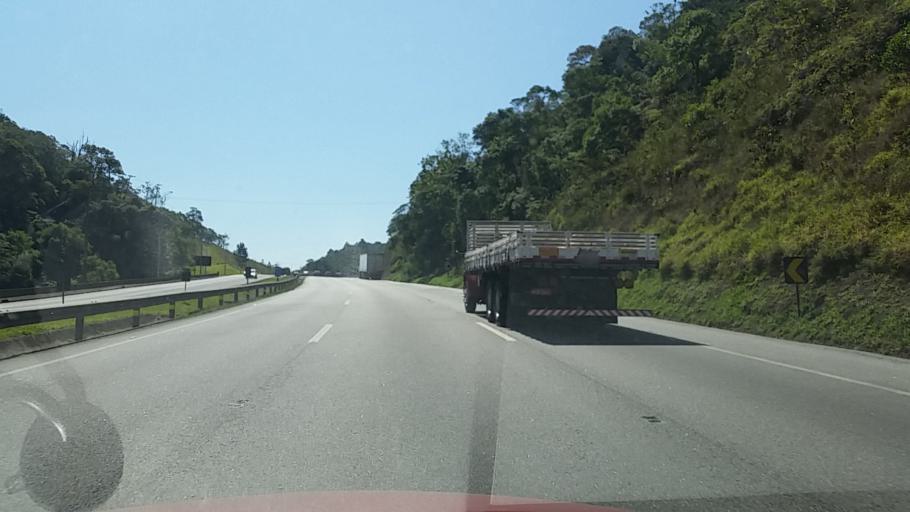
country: BR
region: Sao Paulo
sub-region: Juquitiba
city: Juquitiba
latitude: -23.9923
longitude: -47.1475
